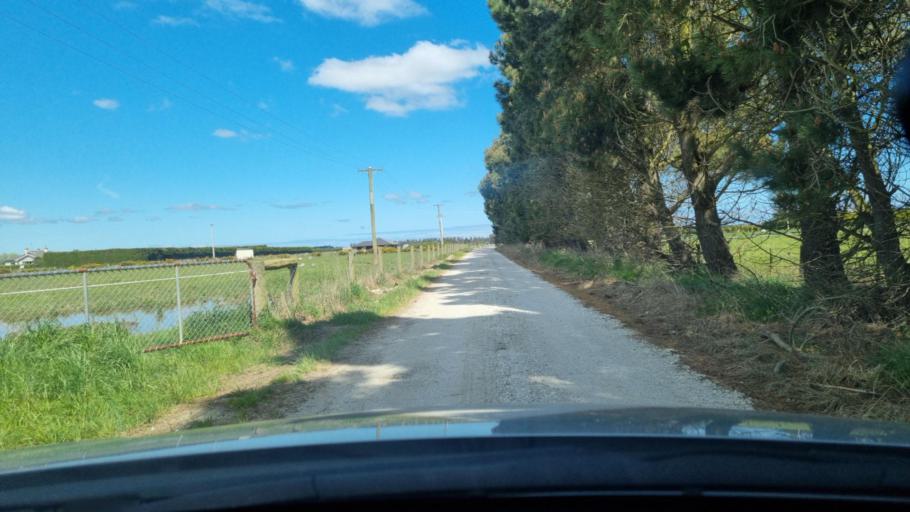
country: NZ
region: Southland
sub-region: Invercargill City
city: Invercargill
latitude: -46.3677
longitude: 168.2827
